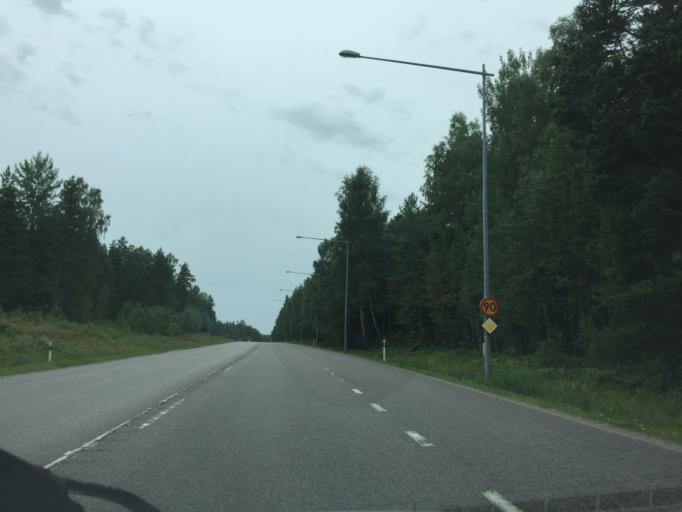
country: SE
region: OErebro
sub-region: Orebro Kommun
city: Orebro
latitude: 59.2426
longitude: 15.2338
